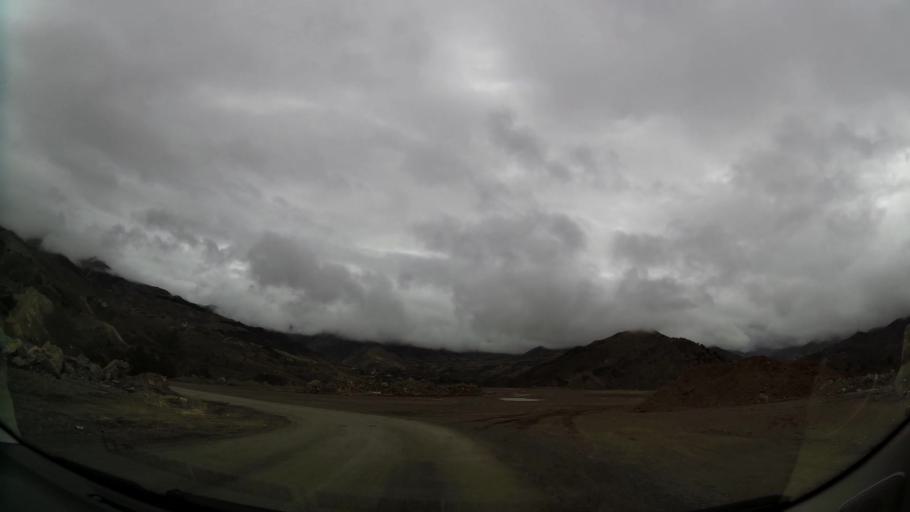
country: MA
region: Taza-Al Hoceima-Taounate
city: Imzourene
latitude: 34.9334
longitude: -3.8131
